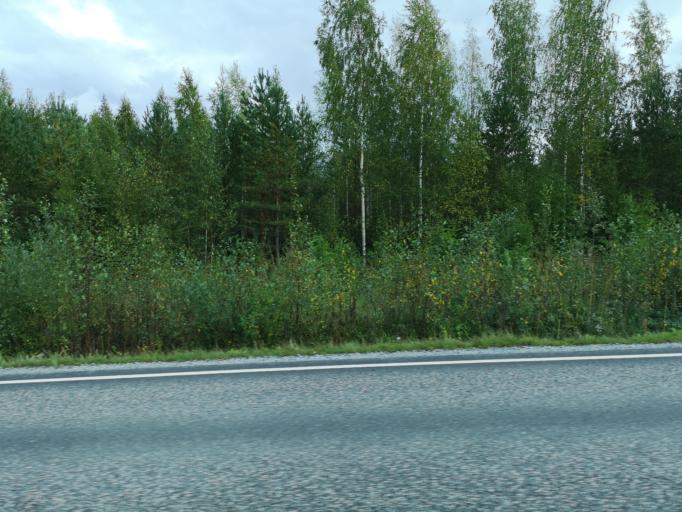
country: FI
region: Central Finland
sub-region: Jyvaeskylae
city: Hankasalmi
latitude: 62.3569
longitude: 26.4534
